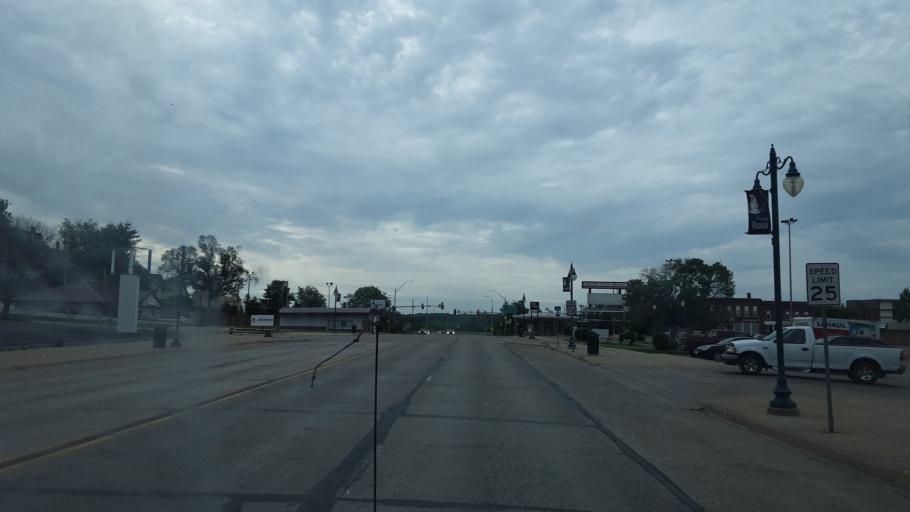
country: US
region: Iowa
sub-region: Lee County
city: Keokuk
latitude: 40.3947
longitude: -91.3822
